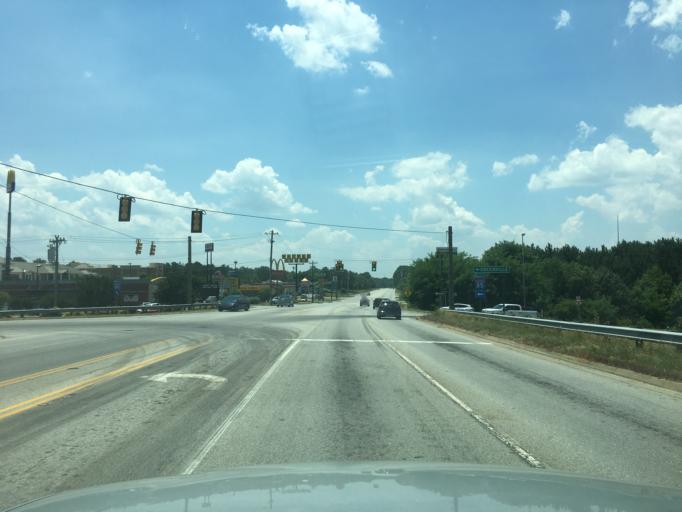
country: US
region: South Carolina
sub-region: Anderson County
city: Northlake
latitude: 34.6320
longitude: -82.5995
